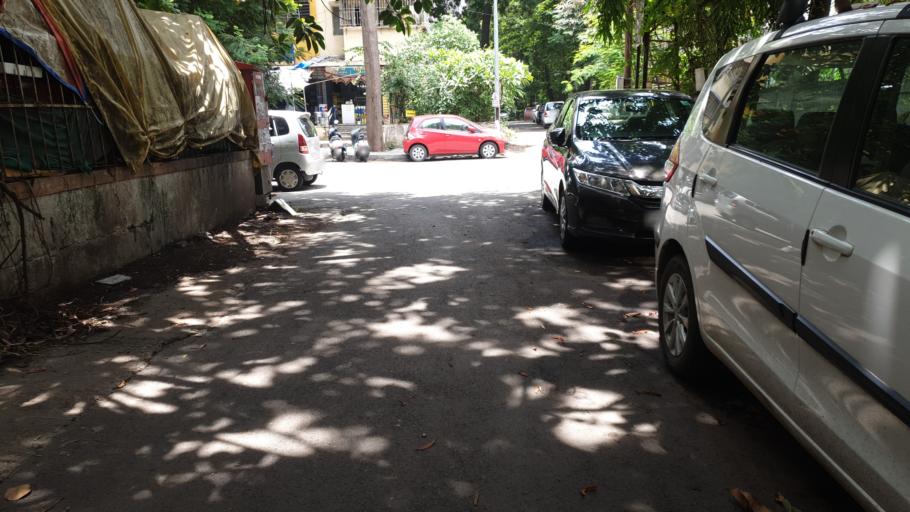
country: IN
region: Maharashtra
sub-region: Pune Division
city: Pune
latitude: 18.4930
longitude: 73.8260
